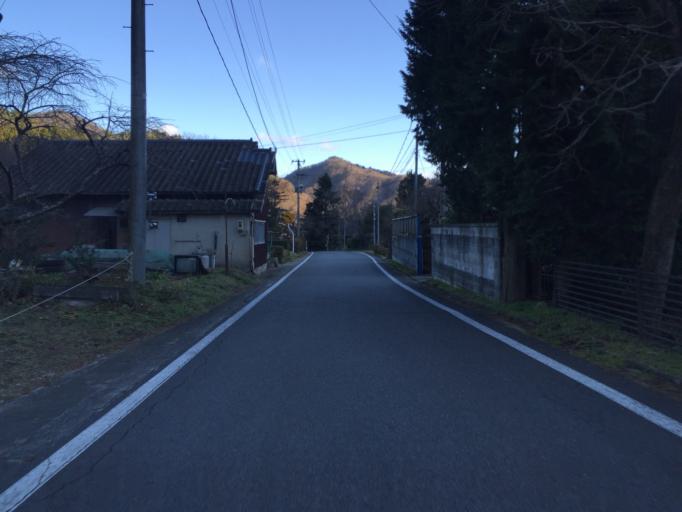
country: JP
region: Fukushima
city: Iwaki
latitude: 37.1836
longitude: 140.8176
